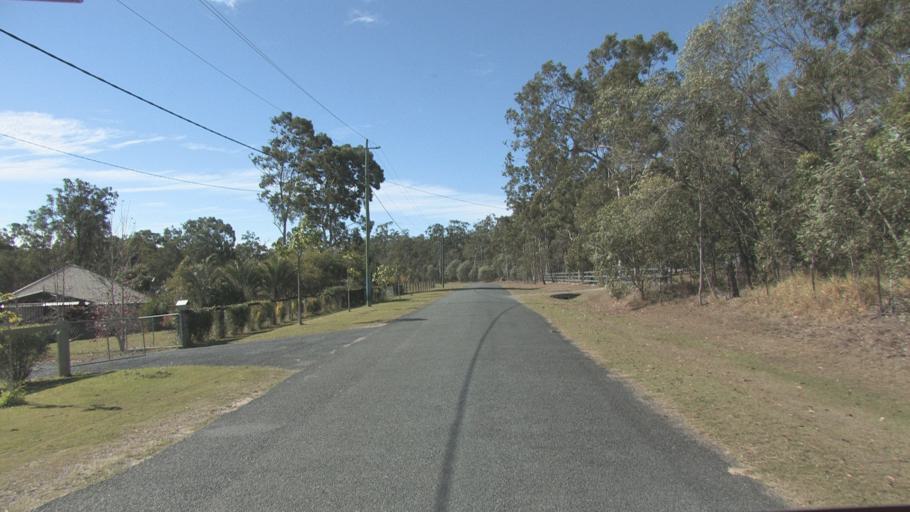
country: AU
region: Queensland
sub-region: Ipswich
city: Springfield Lakes
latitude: -27.7124
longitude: 152.9552
